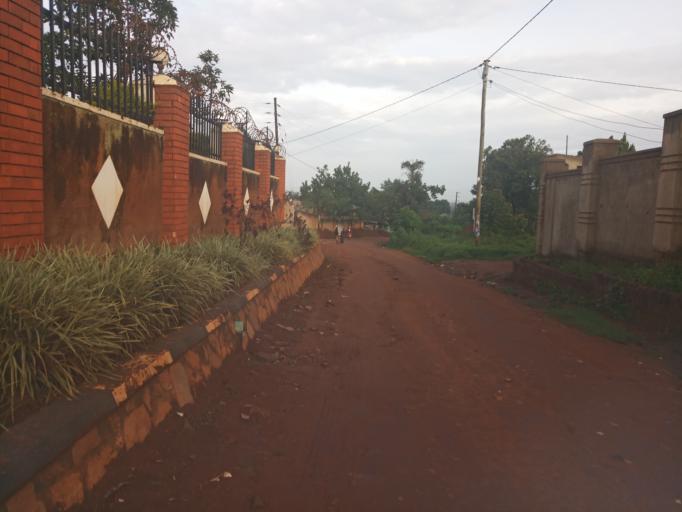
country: UG
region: Central Region
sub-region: Wakiso District
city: Kireka
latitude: 0.3936
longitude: 32.6352
